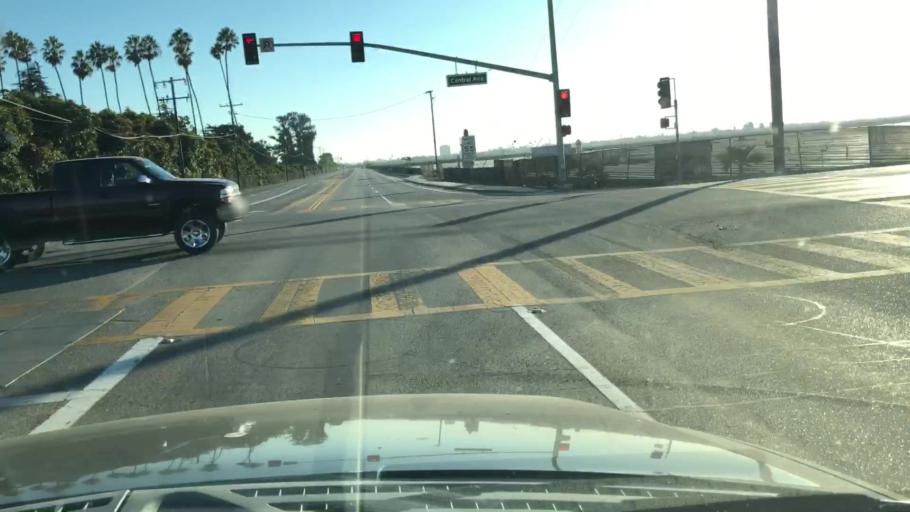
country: US
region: California
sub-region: Ventura County
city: El Rio
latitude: 34.2509
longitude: -119.1425
